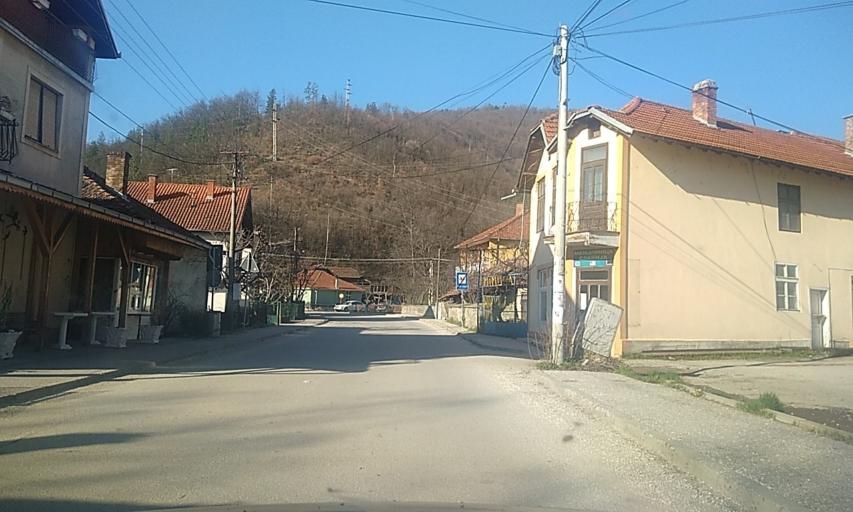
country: RS
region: Central Serbia
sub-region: Pcinjski Okrug
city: Bosilegrad
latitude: 42.4996
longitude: 22.4695
